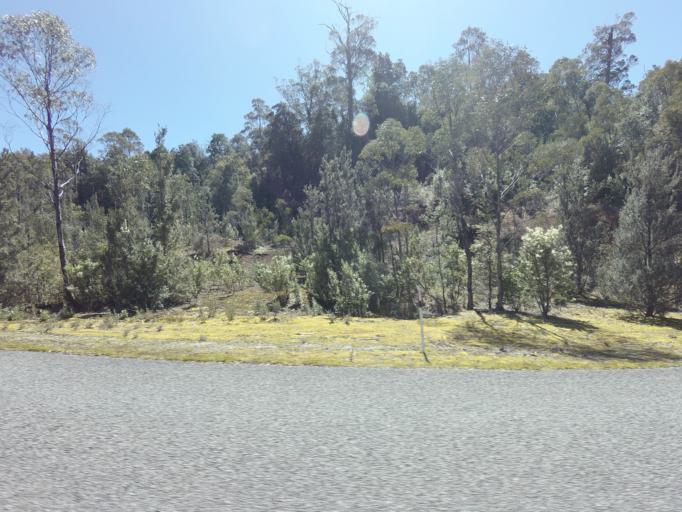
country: AU
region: Tasmania
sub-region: Huon Valley
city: Geeveston
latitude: -42.8167
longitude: 146.3659
